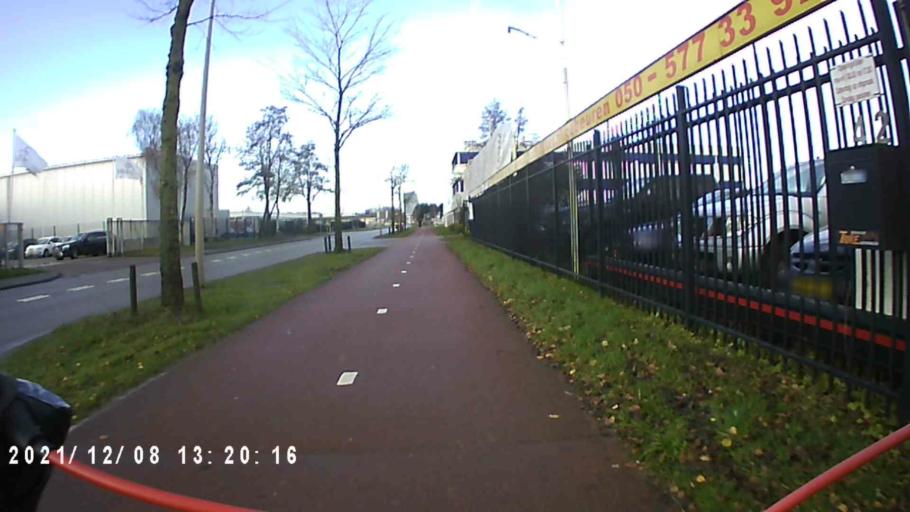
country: NL
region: Groningen
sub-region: Gemeente Haren
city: Haren
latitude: 53.2002
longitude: 6.6026
